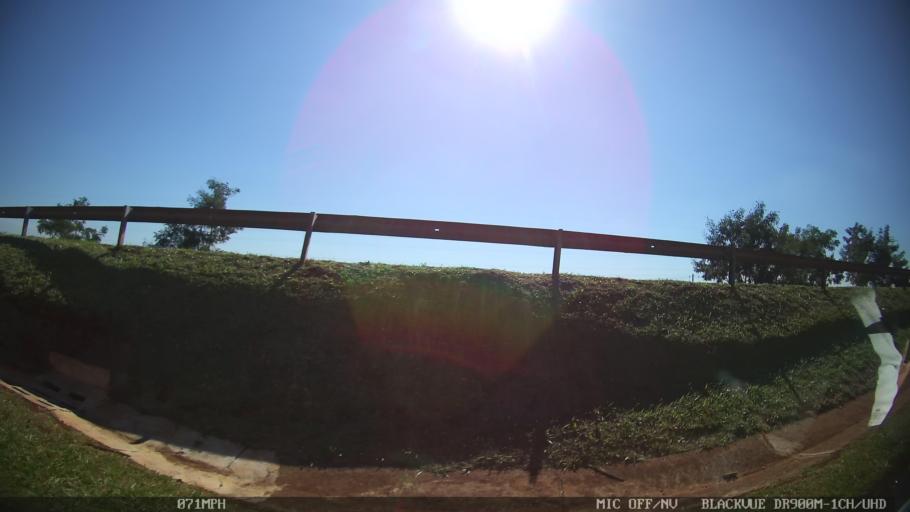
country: BR
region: Sao Paulo
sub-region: Ribeirao Preto
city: Ribeirao Preto
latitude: -21.1367
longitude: -47.8615
